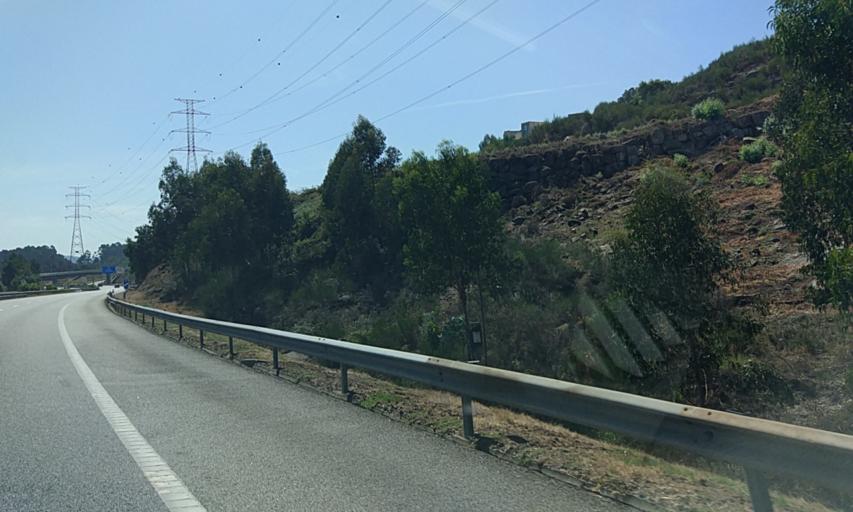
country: PT
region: Porto
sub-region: Paredes
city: Baltar
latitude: 41.1726
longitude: -8.3829
